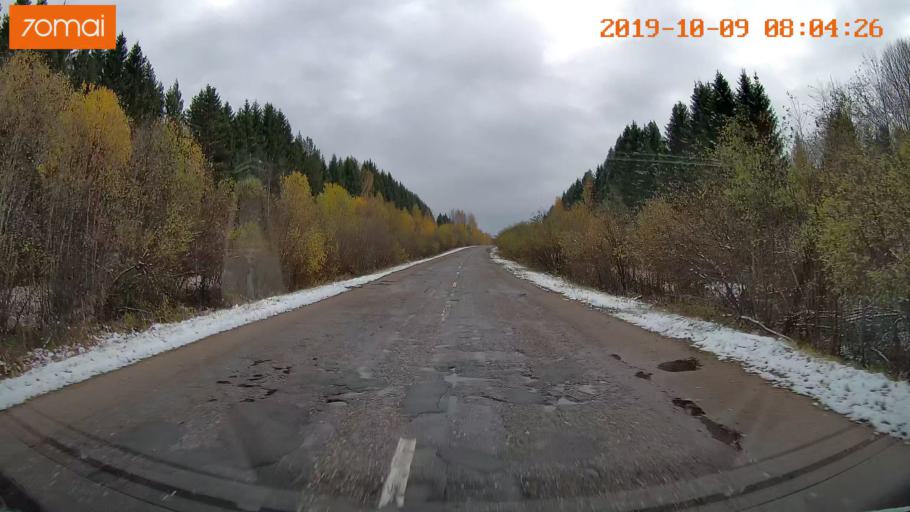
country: RU
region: Jaroslavl
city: Kukoboy
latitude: 58.6916
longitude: 40.0267
